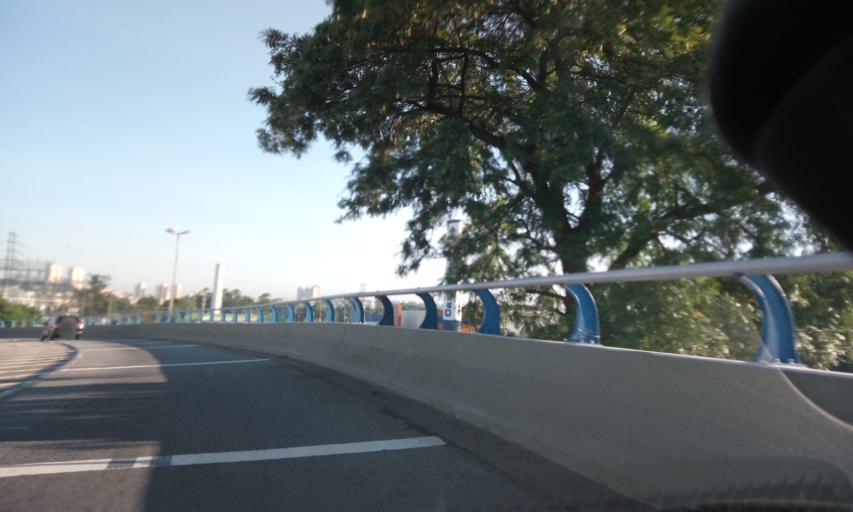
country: BR
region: Sao Paulo
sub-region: Santo Andre
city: Santo Andre
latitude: -23.6642
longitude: -46.5113
